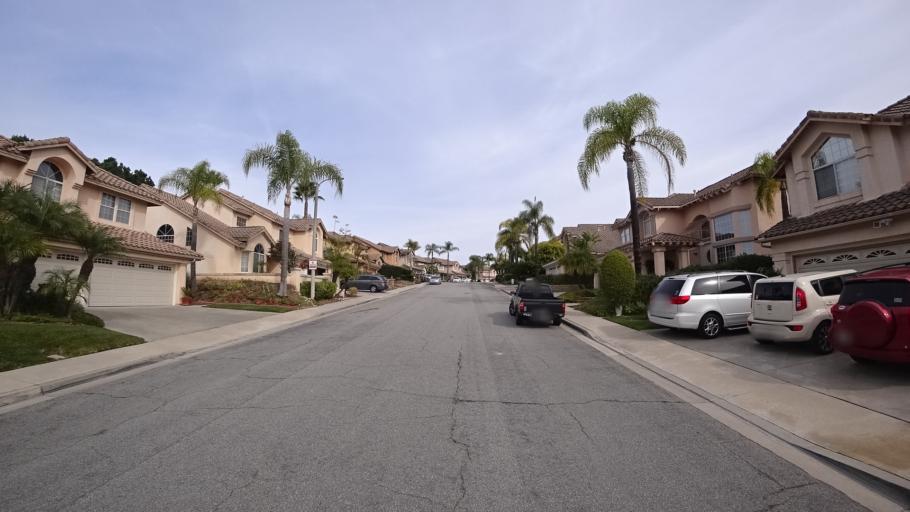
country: US
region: California
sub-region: Orange County
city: Laguna Woods
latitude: 33.5923
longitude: -117.7413
